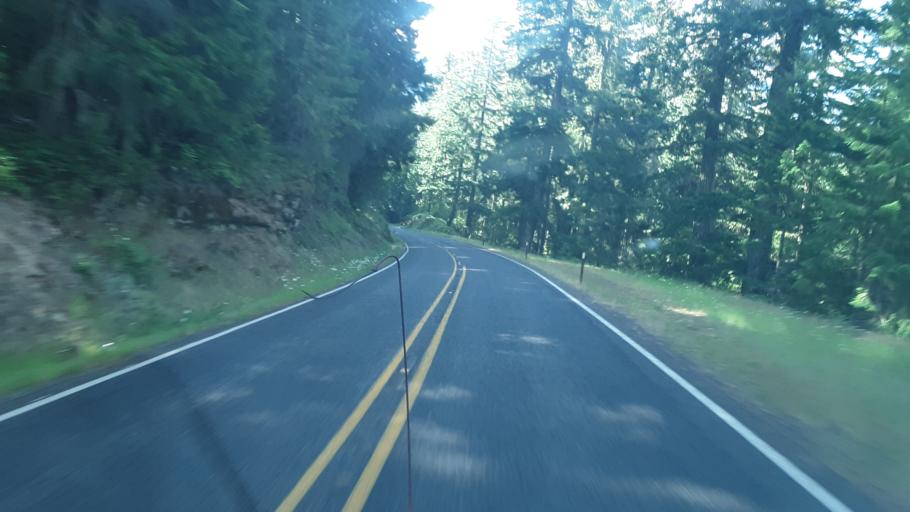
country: US
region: Washington
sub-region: Pierce County
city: Buckley
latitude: 46.6985
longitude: -121.5825
